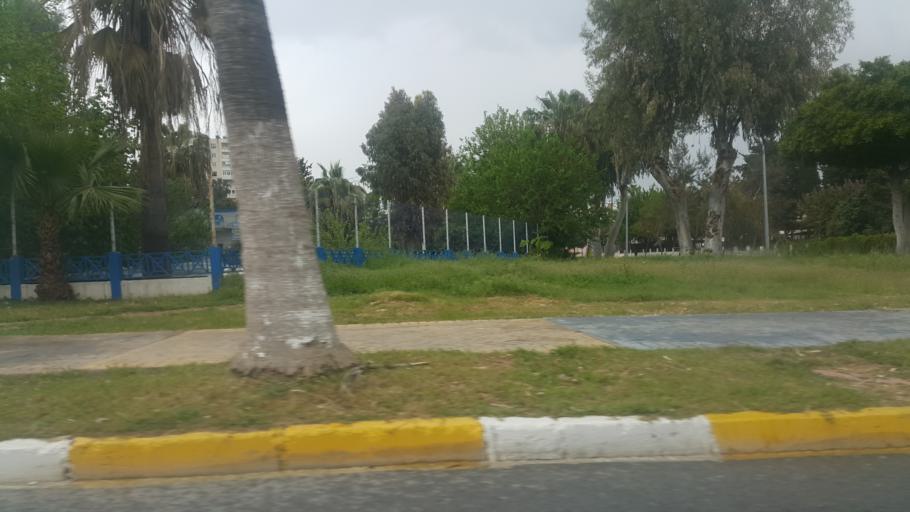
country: TR
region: Mersin
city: Mercin
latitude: 36.7759
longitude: 34.5779
